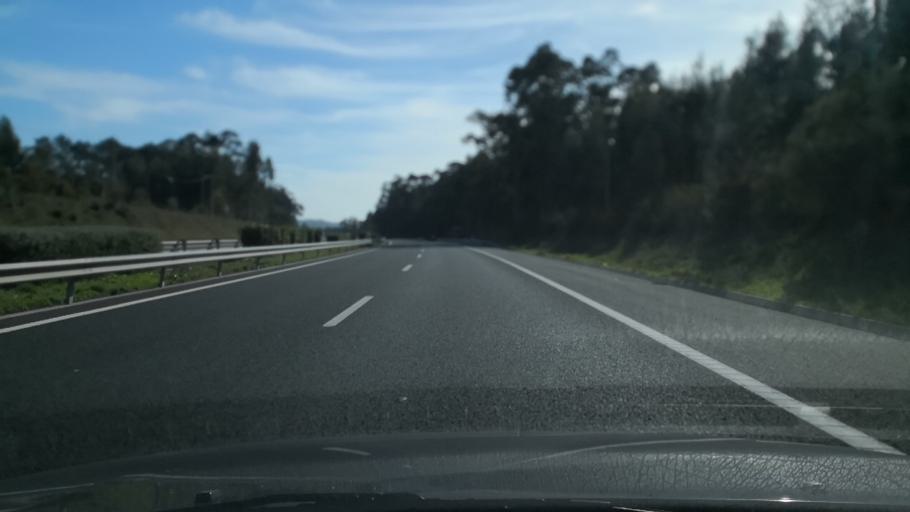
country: PT
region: Leiria
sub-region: Leiria
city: Santa Catarina da Serra
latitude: 39.6567
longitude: -8.6956
